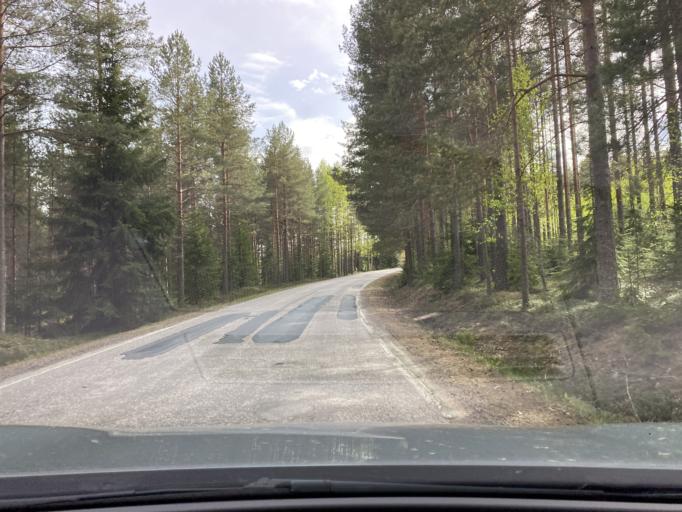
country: FI
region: Varsinais-Suomi
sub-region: Salo
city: Kiikala
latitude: 60.4821
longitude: 23.5402
